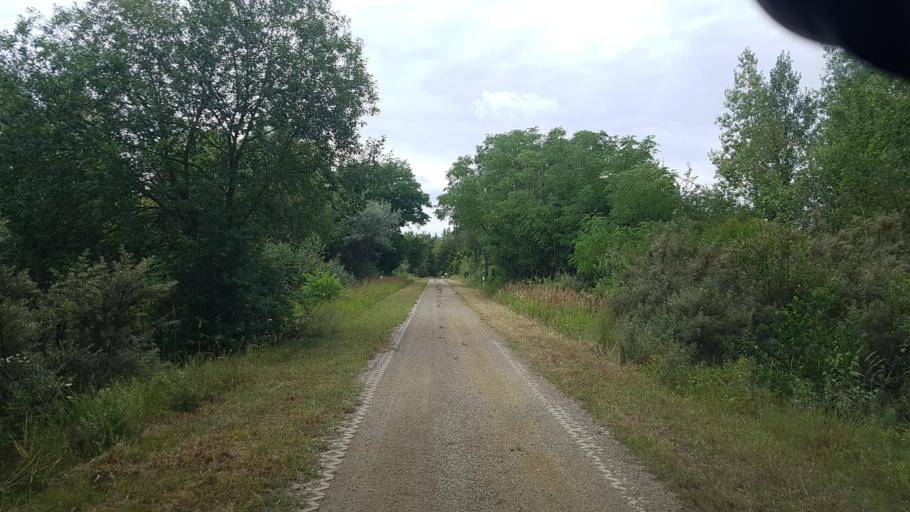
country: DE
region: Brandenburg
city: Spremberg
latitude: 51.5823
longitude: 14.3119
